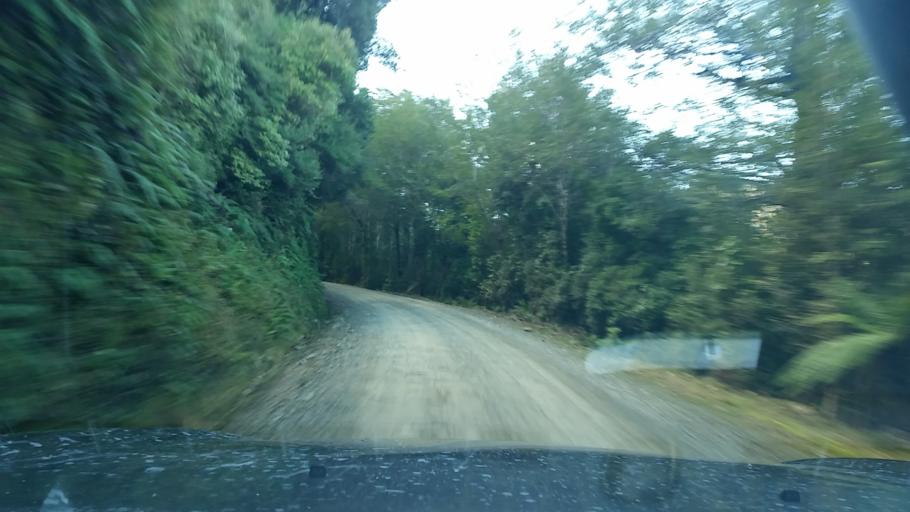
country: NZ
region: Marlborough
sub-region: Marlborough District
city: Picton
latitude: -41.0917
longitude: 174.1363
